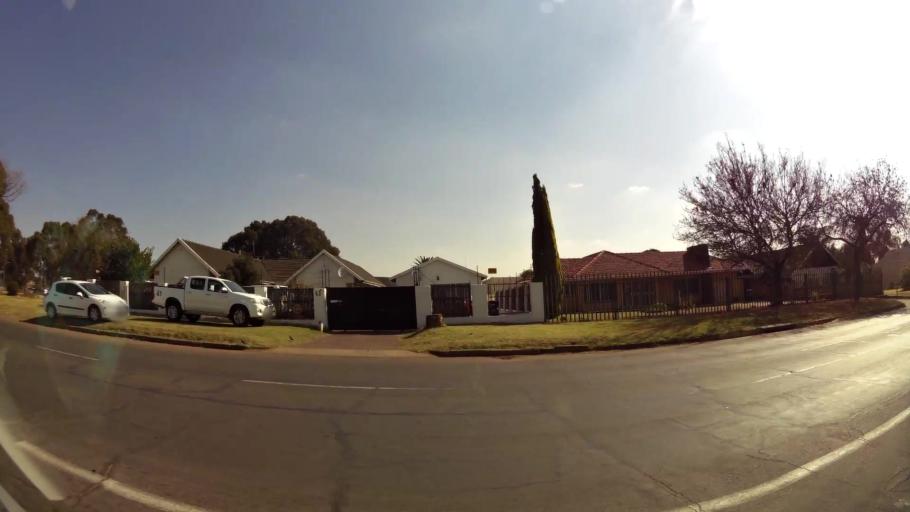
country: ZA
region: Gauteng
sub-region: City of Johannesburg Metropolitan Municipality
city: Modderfontein
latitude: -26.1189
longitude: 28.2329
